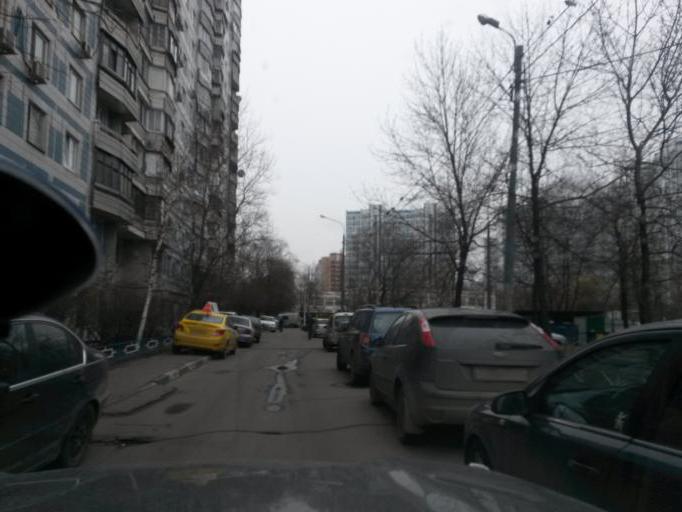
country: RU
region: Moscow
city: Brateyevo
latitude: 55.6382
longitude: 37.7513
